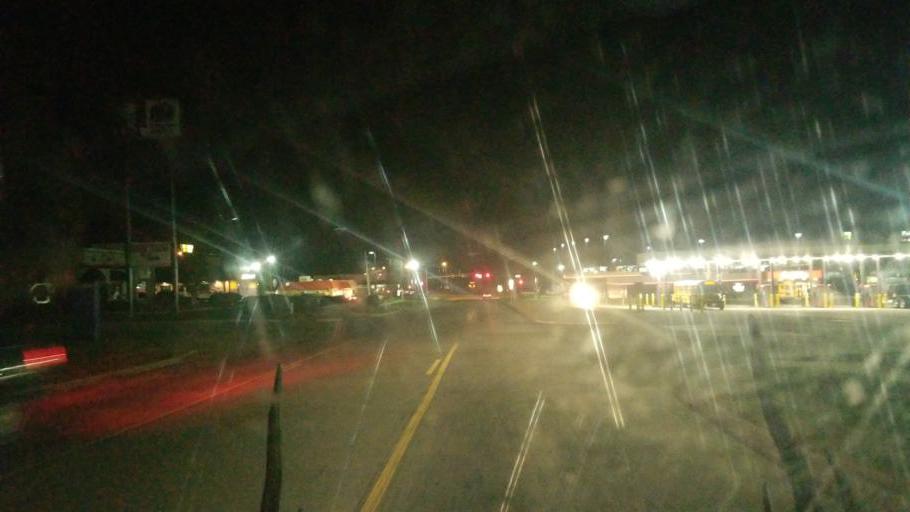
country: US
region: Missouri
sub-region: Jackson County
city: Oak Grove
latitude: 39.0128
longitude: -94.1263
